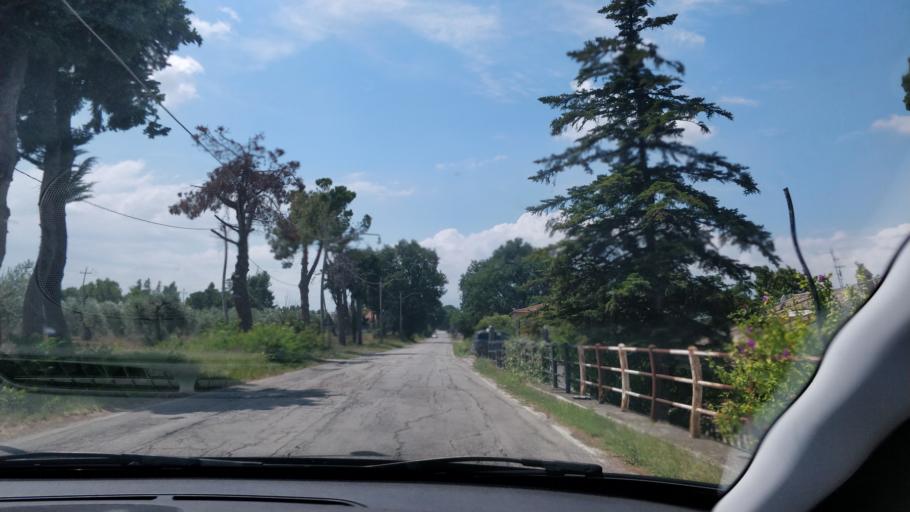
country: IT
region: Abruzzo
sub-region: Provincia di Chieti
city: Torrevecchia
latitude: 42.3941
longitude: 14.2033
